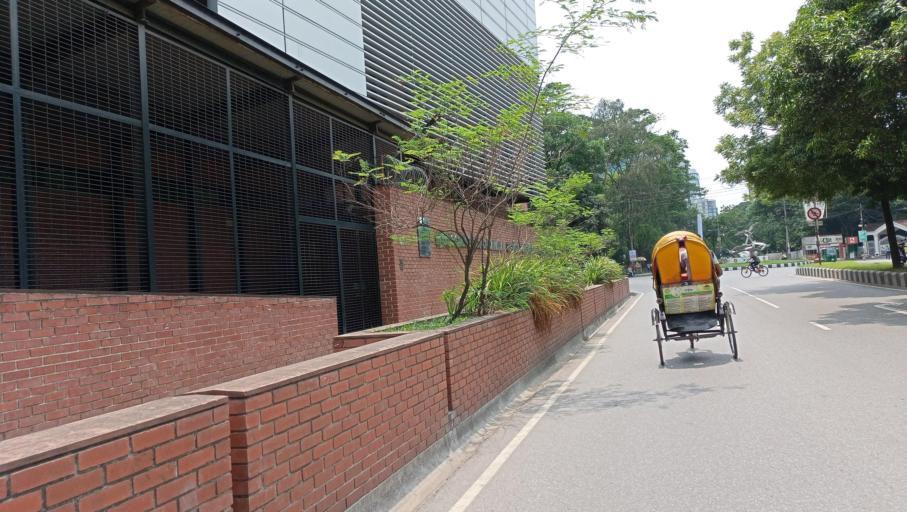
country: BD
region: Dhaka
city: Paltan
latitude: 23.7969
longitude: 90.4205
